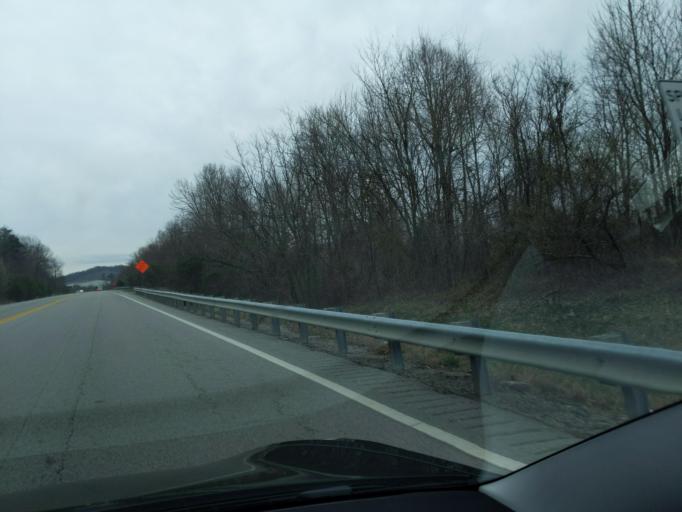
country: US
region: Kentucky
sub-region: Whitley County
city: Corbin
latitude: 36.9141
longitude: -84.0698
